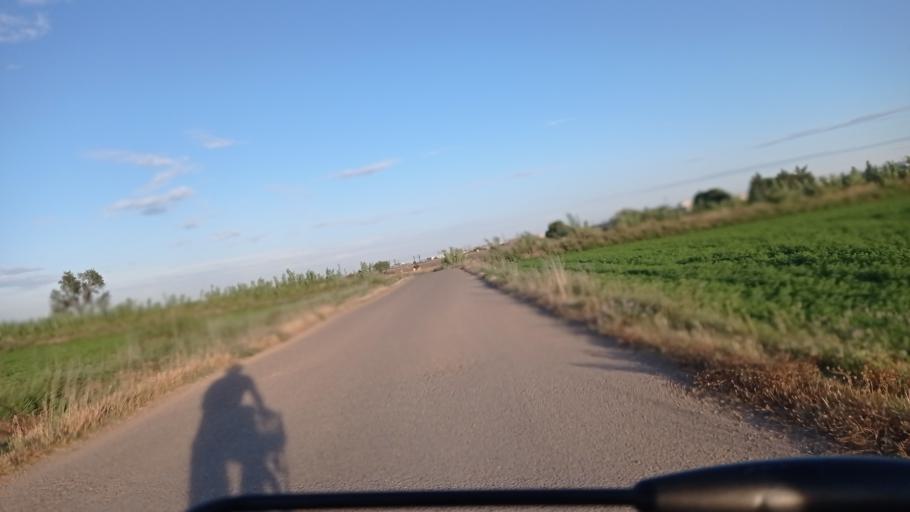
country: ES
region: Aragon
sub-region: Provincia de Zaragoza
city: Oliver-Valdefierro, Oliver, Valdefierro
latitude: 41.6749
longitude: -0.9436
